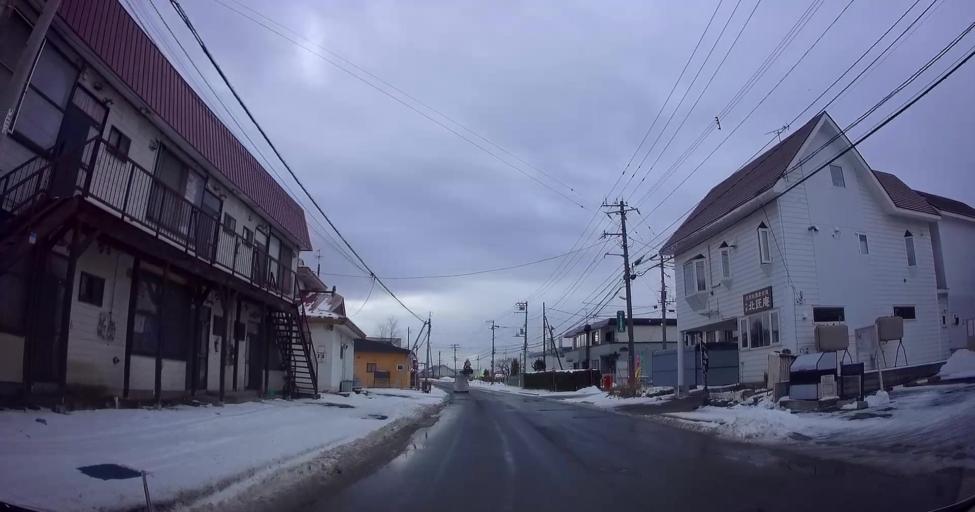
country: JP
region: Hokkaido
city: Kamiiso
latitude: 41.8272
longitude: 140.6860
